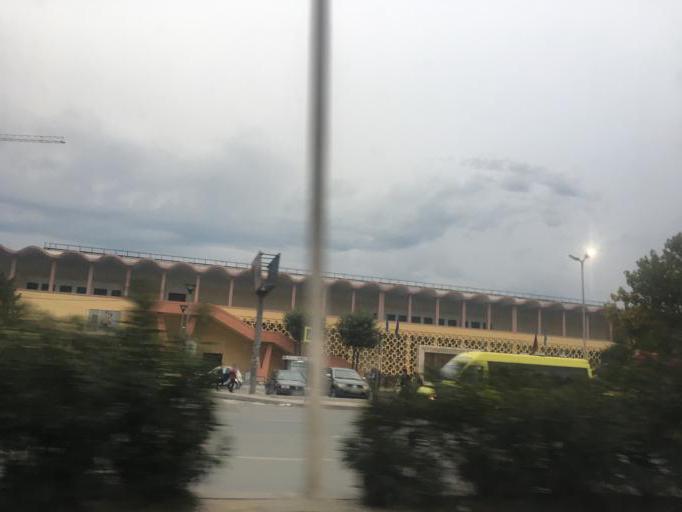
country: AL
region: Tirane
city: Tirana
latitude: 41.3337
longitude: 19.8024
